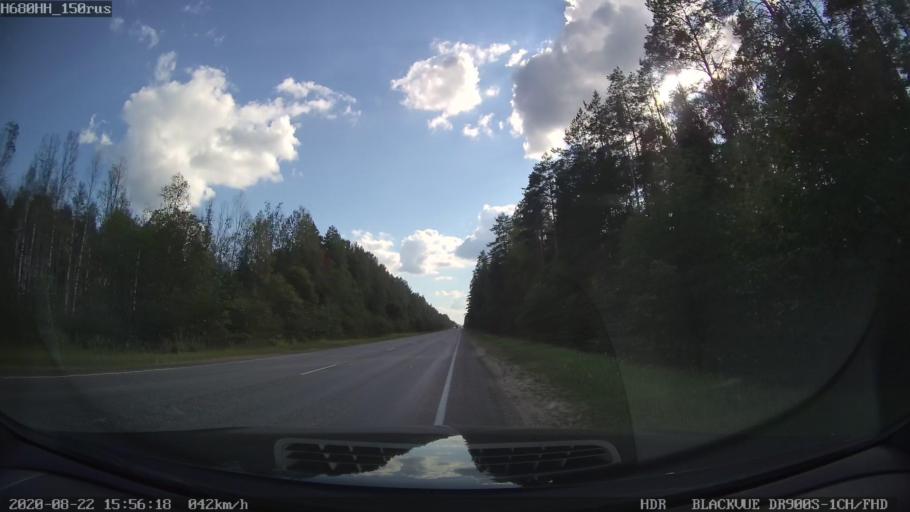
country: RU
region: Tverskaya
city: Bezhetsk
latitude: 57.6113
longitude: 36.3644
